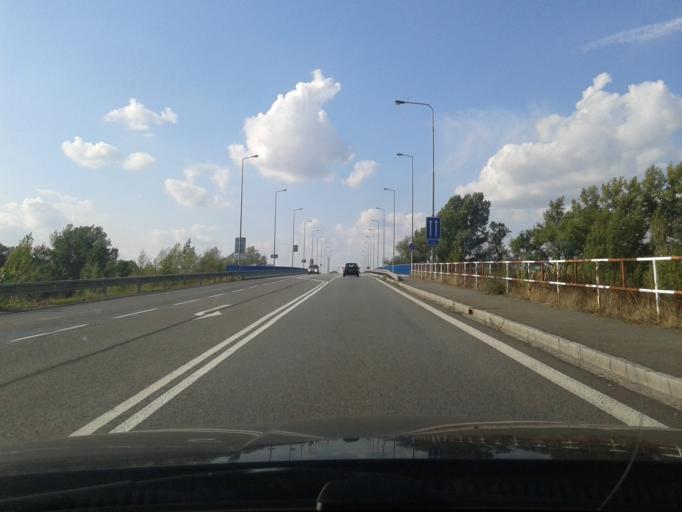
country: CZ
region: Moravskoslezsky
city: Stary Bohumin
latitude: 49.9154
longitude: 18.3251
